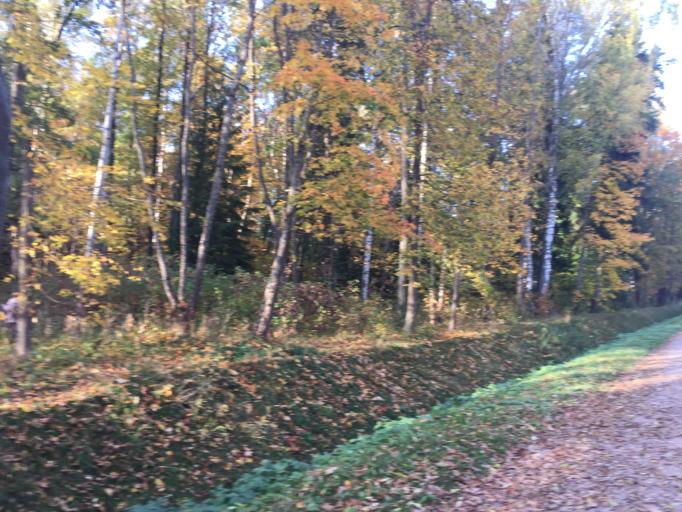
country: RU
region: St.-Petersburg
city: Pushkin
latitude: 59.7236
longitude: 30.3797
